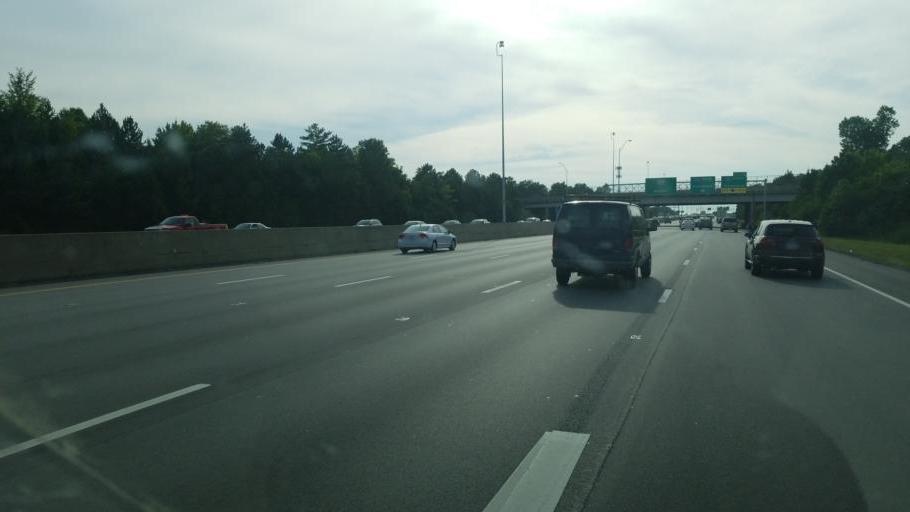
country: US
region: Ohio
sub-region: Franklin County
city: Minerva Park
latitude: 40.1076
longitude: -82.9594
